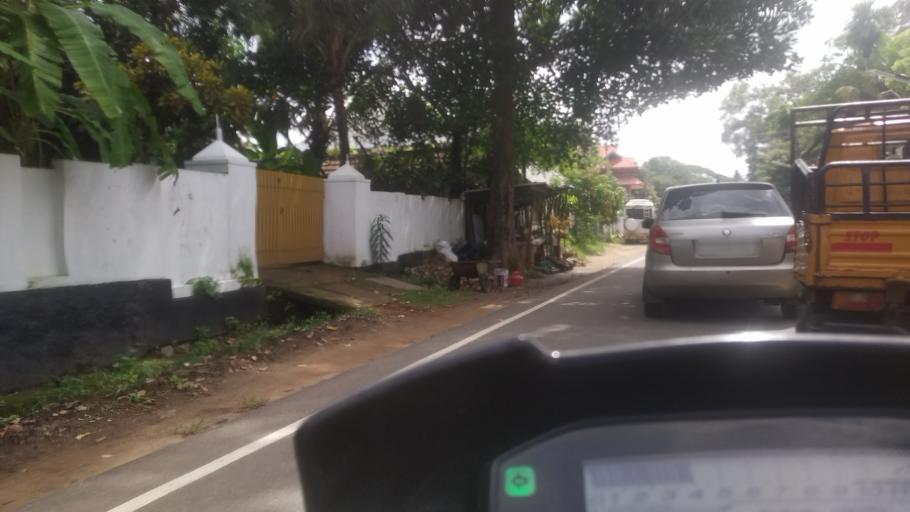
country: IN
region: Kerala
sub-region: Ernakulam
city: Elur
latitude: 10.1322
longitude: 76.2784
